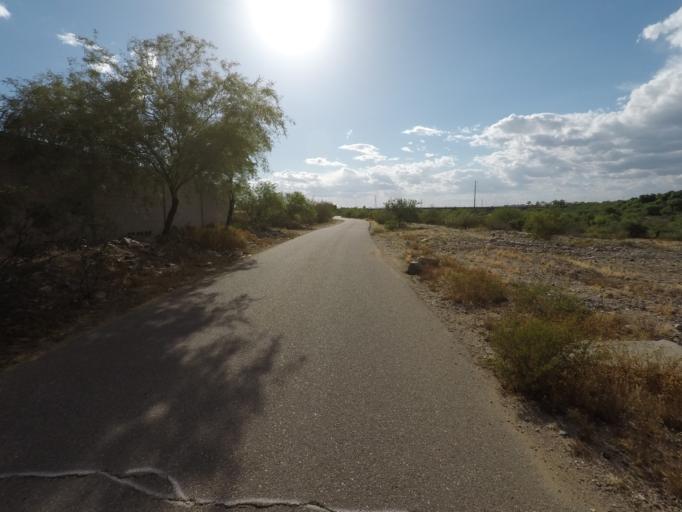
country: US
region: Arizona
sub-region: Maricopa County
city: Phoenix
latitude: 33.4198
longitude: -112.0680
